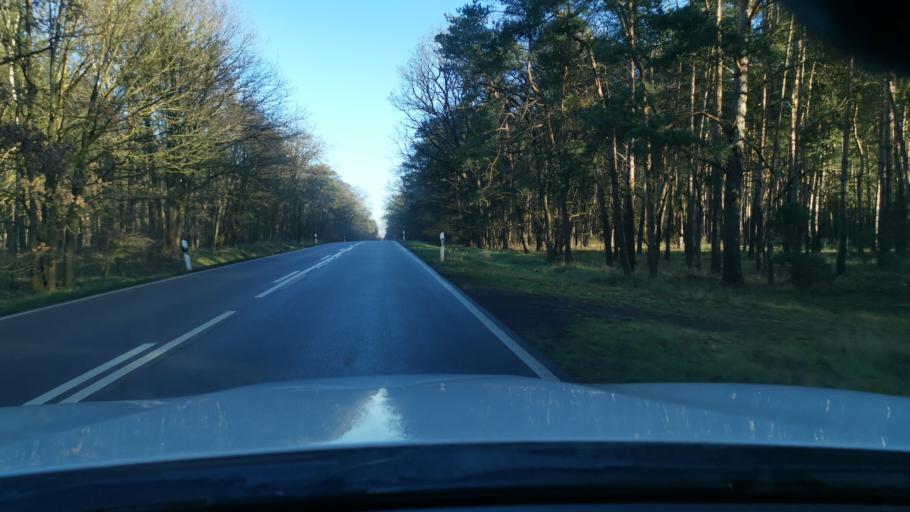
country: DE
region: Saxony-Anhalt
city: Abtsdorf
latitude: 51.9242
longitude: 12.7019
